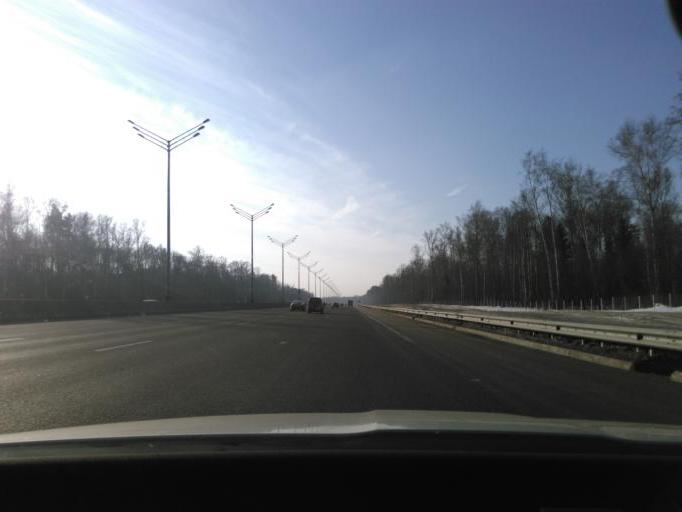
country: RU
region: Moscow
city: Khimki
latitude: 55.9303
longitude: 37.4524
